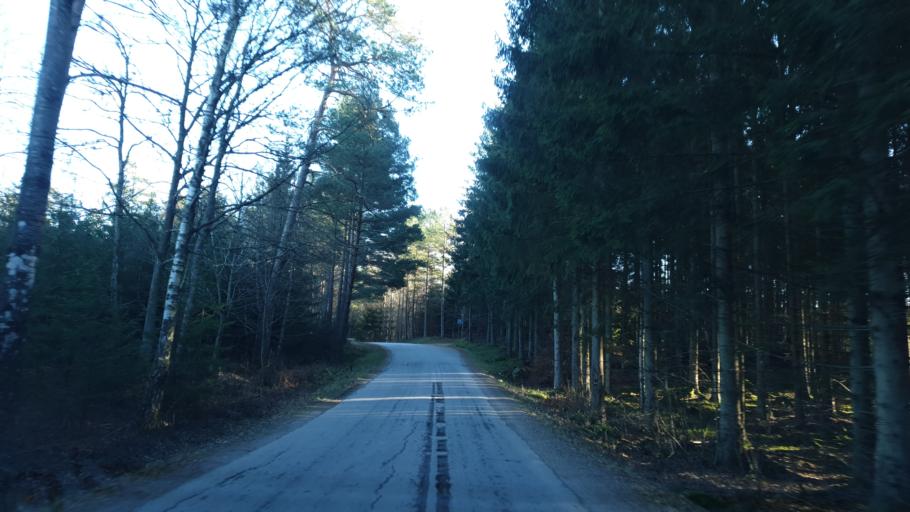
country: SE
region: Blekinge
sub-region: Ronneby Kommun
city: Brakne-Hoby
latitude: 56.2316
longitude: 15.1594
